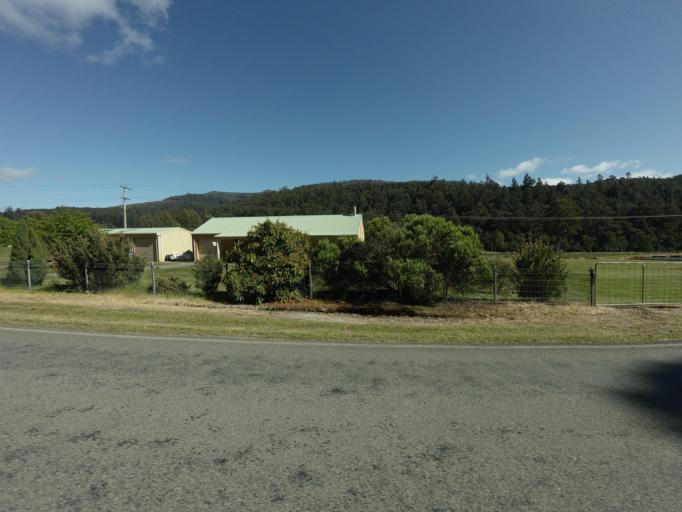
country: AU
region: Tasmania
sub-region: Derwent Valley
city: New Norfolk
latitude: -42.7230
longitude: 146.6786
